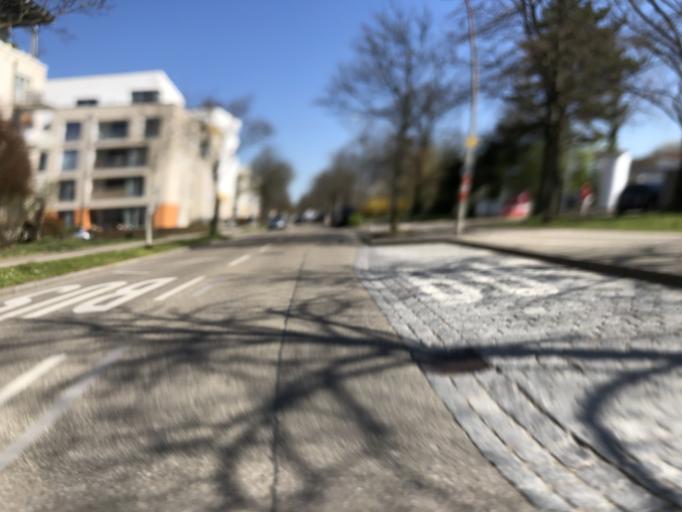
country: DE
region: Baden-Wuerttemberg
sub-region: Freiburg Region
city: Merzhausen
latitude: 47.9857
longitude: 7.8114
